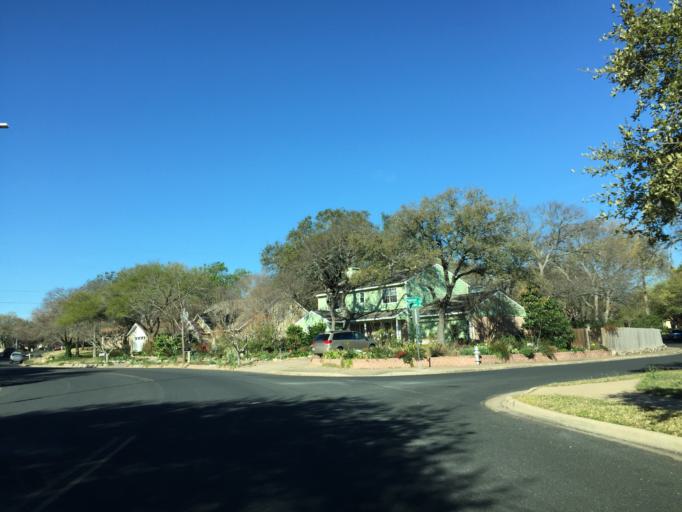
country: US
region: Texas
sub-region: Williamson County
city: Jollyville
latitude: 30.4061
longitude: -97.7325
